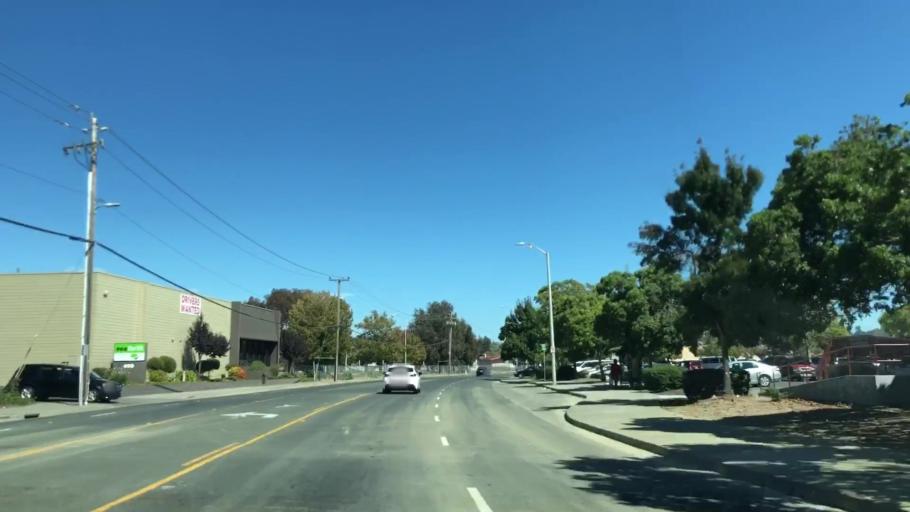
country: US
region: California
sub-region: Solano County
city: Vallejo
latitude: 38.1231
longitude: -122.2594
